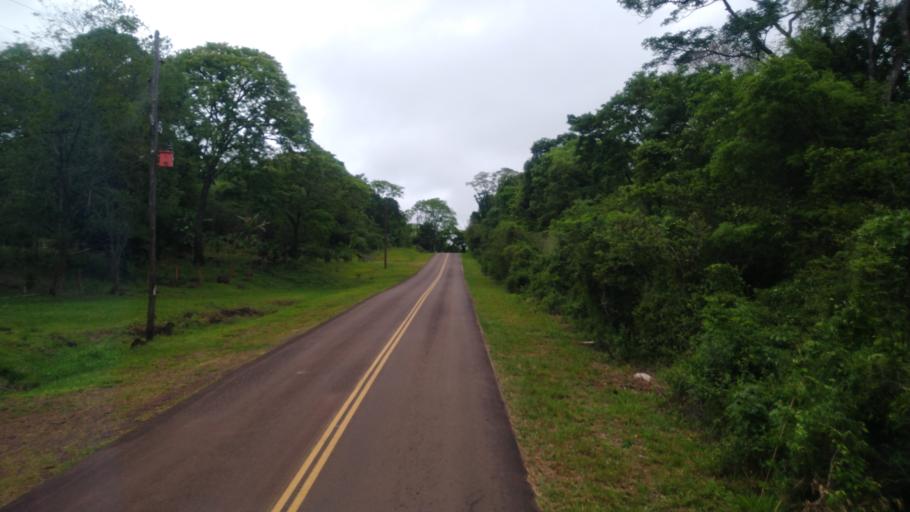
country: AR
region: Misiones
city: Santa Ana
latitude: -27.4393
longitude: -55.5706
